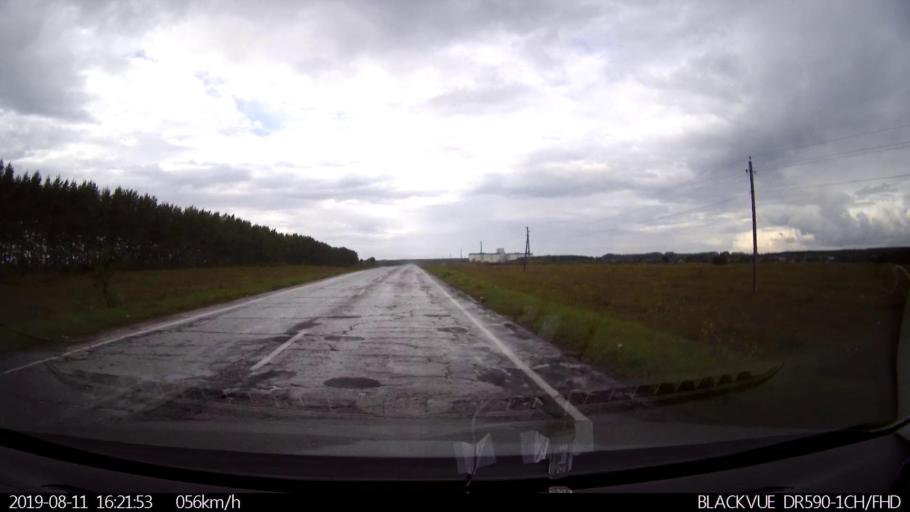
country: RU
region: Ulyanovsk
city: Mayna
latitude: 54.0833
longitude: 47.5958
